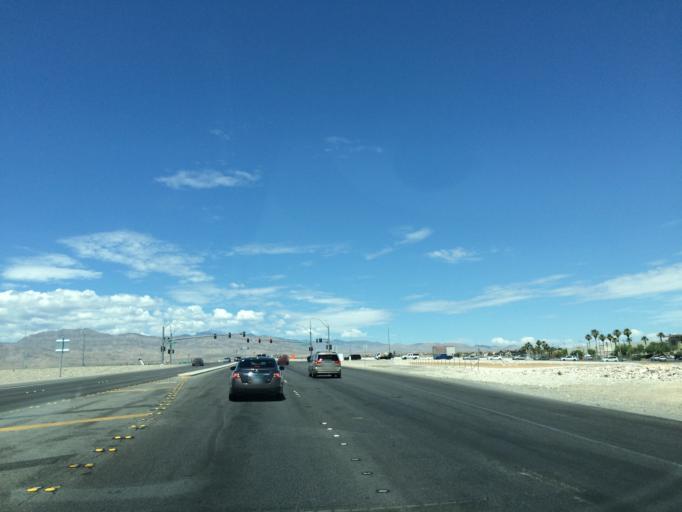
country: US
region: Nevada
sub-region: Clark County
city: Las Vegas
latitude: 36.2772
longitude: -115.2607
